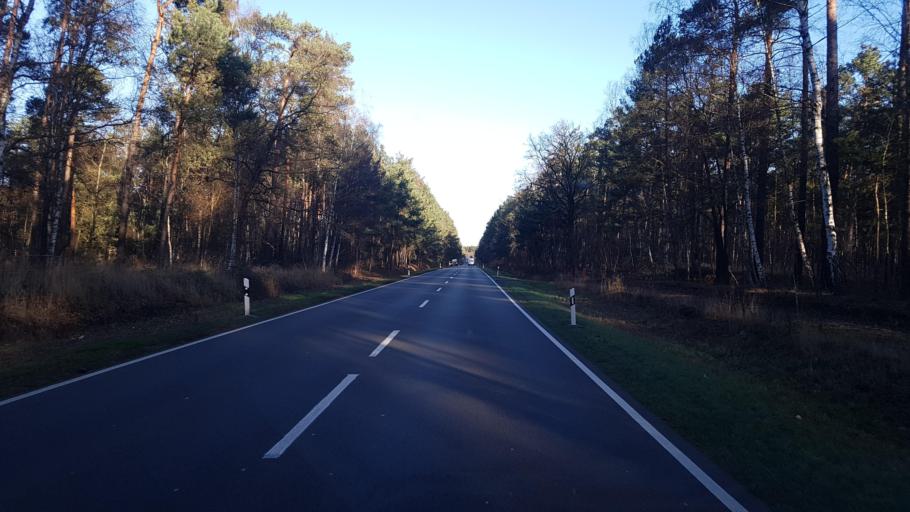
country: DE
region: Brandenburg
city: Heinersbruck
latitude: 51.7185
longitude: 14.4584
